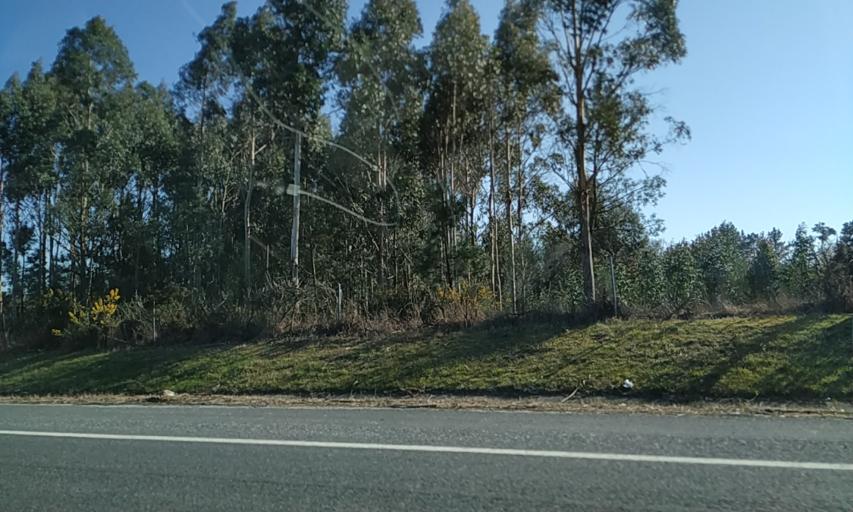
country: ES
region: Galicia
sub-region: Provincia da Coruna
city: Aranga
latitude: 43.2116
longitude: -8.0468
